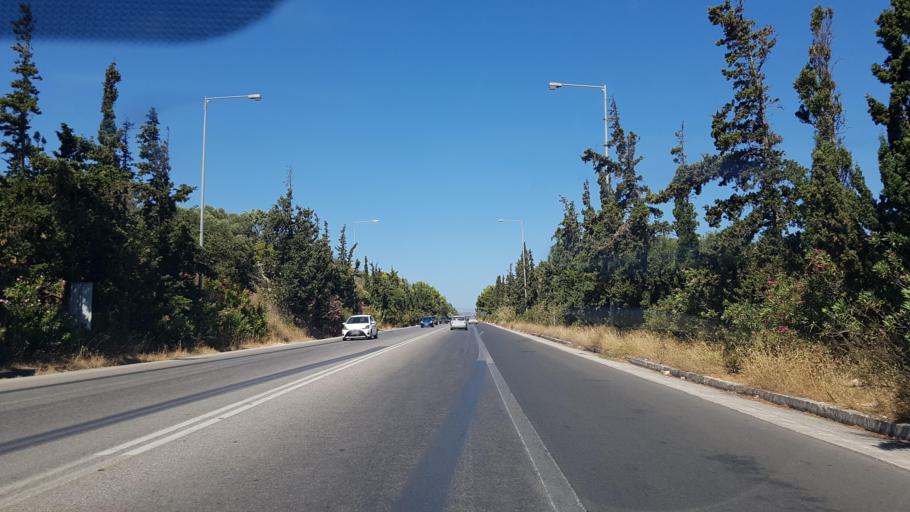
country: GR
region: Crete
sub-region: Nomos Chanias
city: Gerani
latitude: 35.5122
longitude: 23.8866
